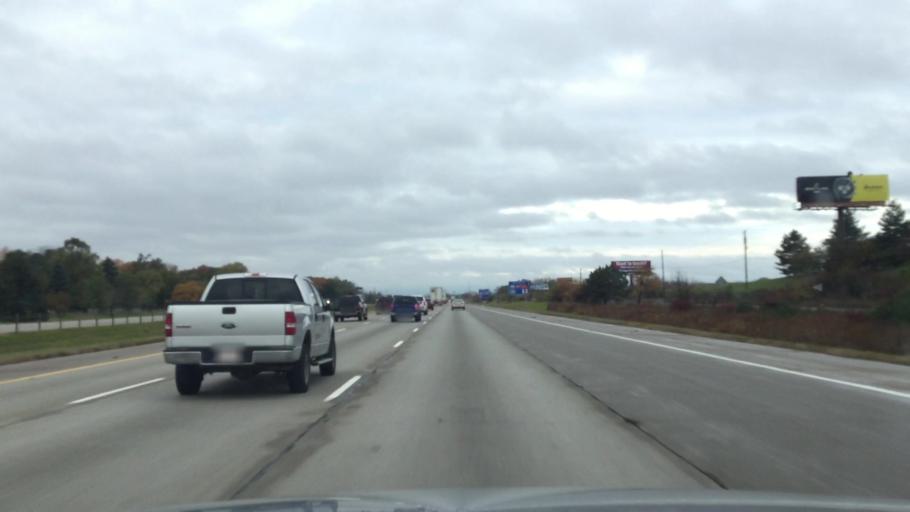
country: US
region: Michigan
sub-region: Wayne County
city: Belleville
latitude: 42.2190
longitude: -83.5257
